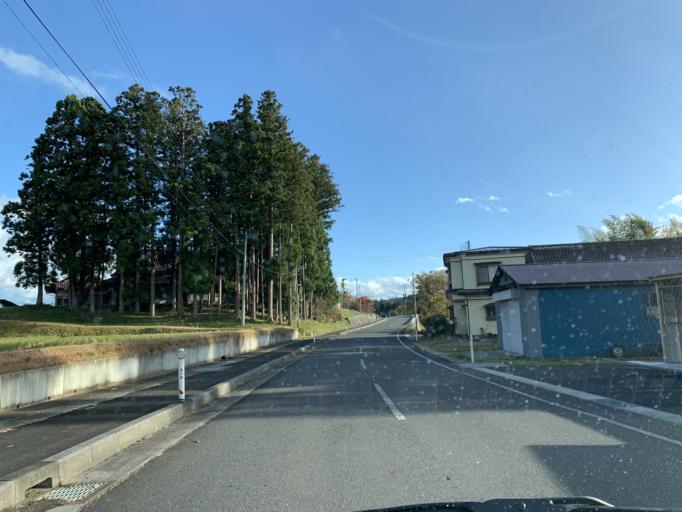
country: JP
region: Iwate
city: Ichinoseki
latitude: 39.0203
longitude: 141.0873
